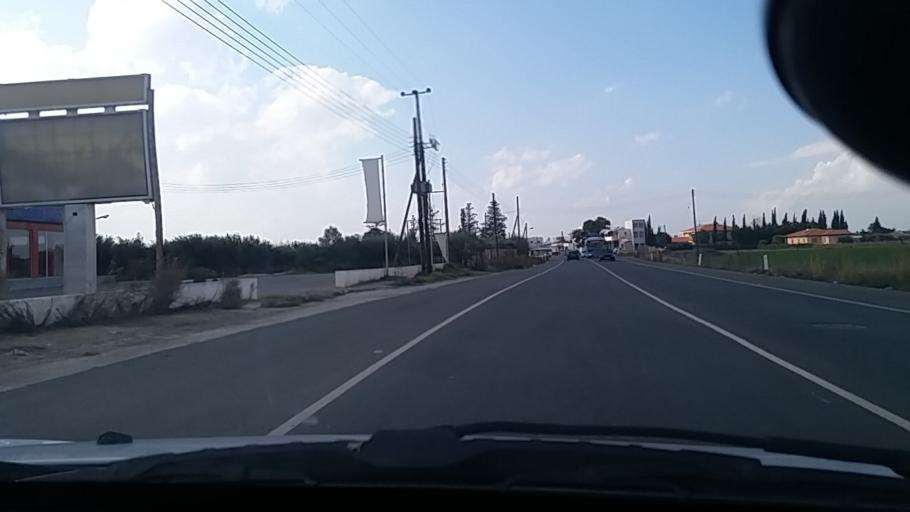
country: CY
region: Lefkosia
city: Kokkinotrimithia
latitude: 35.1489
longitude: 33.2178
